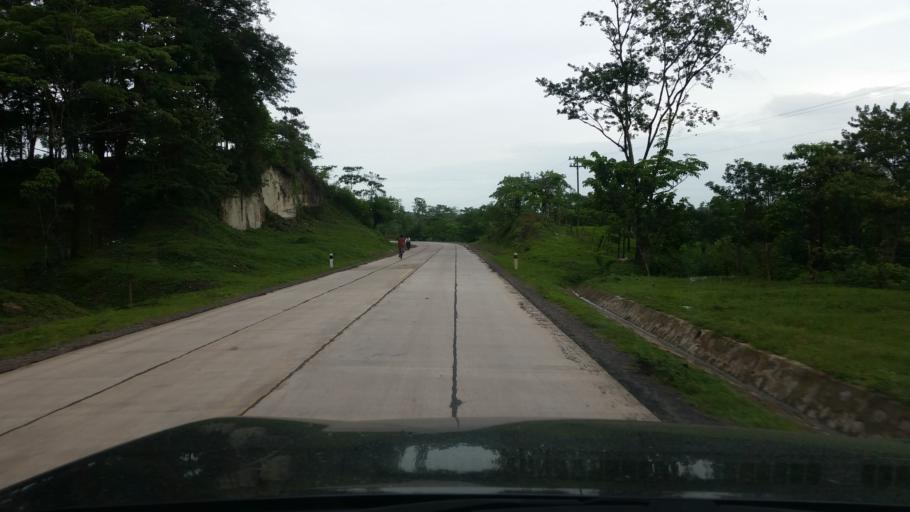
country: NI
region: Matagalpa
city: Rio Blanco
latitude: 13.1576
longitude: -84.9721
